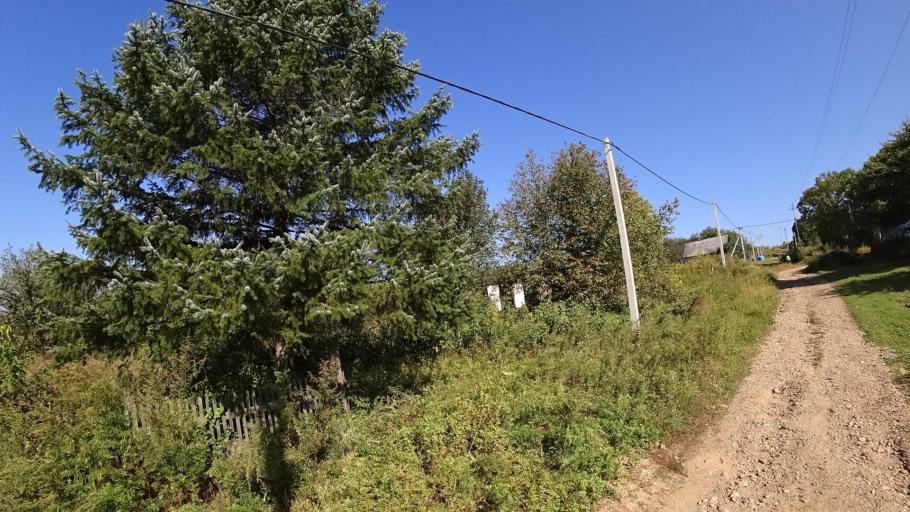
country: RU
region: Jewish Autonomous Oblast
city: Bira
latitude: 49.0076
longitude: 132.4680
